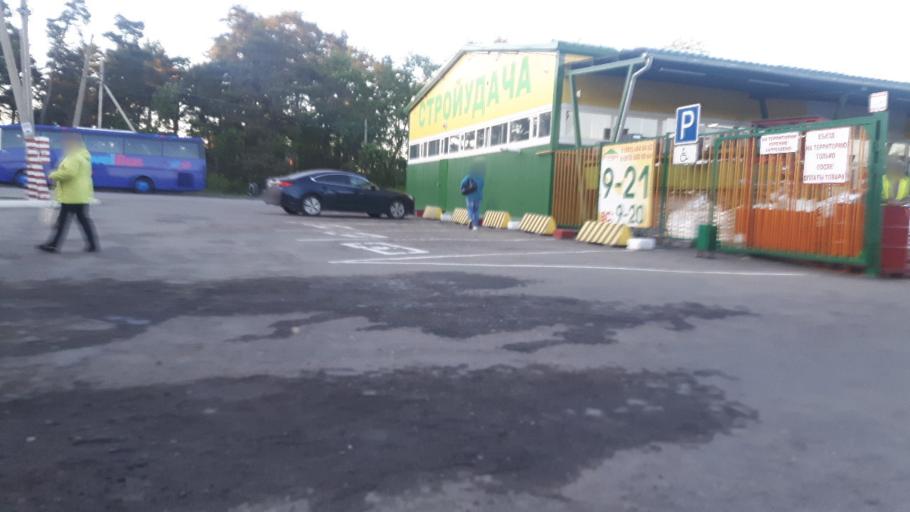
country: RU
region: St.-Petersburg
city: Bol'shaya Izhora
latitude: 59.9439
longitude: 29.5740
